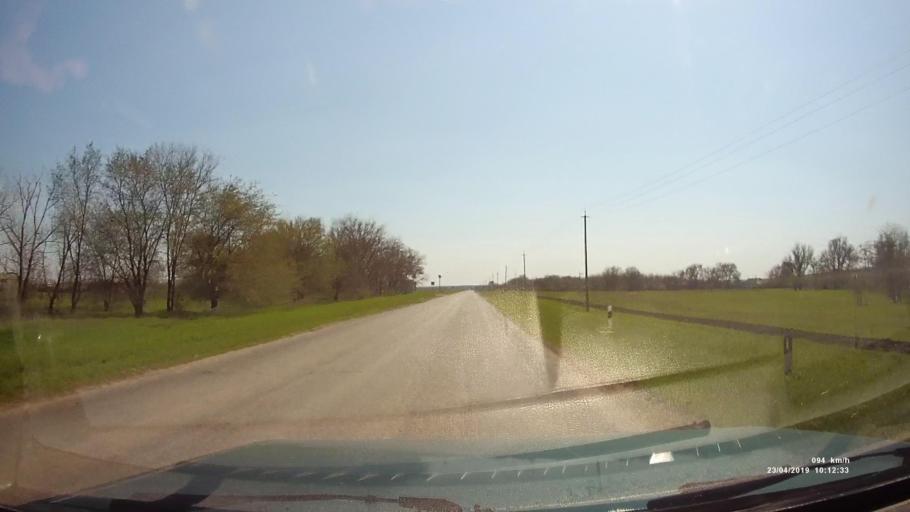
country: RU
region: Rostov
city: Sovetskoye
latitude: 46.6896
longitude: 42.3378
